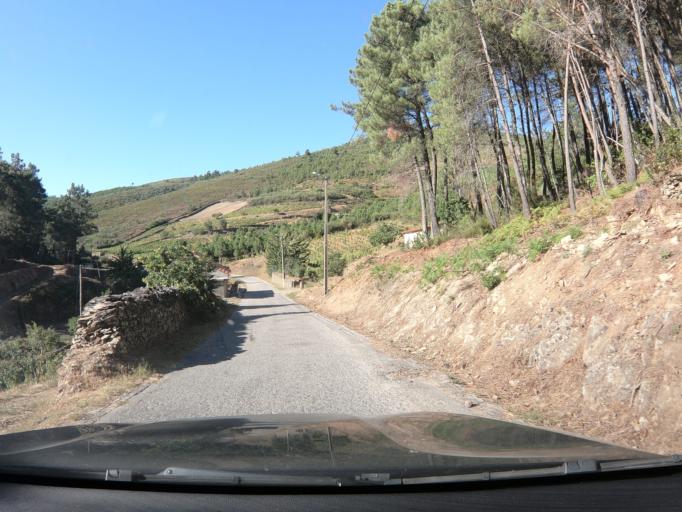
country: PT
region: Vila Real
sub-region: Sabrosa
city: Vilela
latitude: 41.2241
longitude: -7.5819
